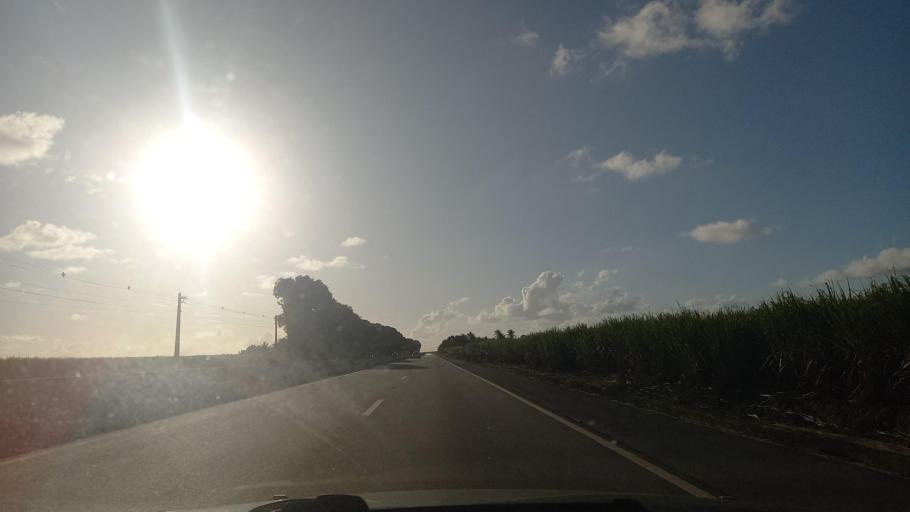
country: BR
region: Alagoas
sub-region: Campo Alegre
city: Campo Alegre
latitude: -9.8201
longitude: -36.2461
